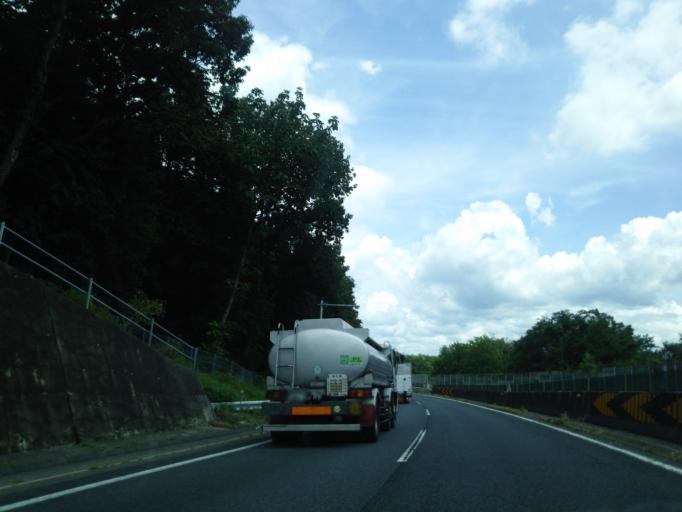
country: JP
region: Gifu
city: Toki
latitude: 35.3701
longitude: 137.2031
